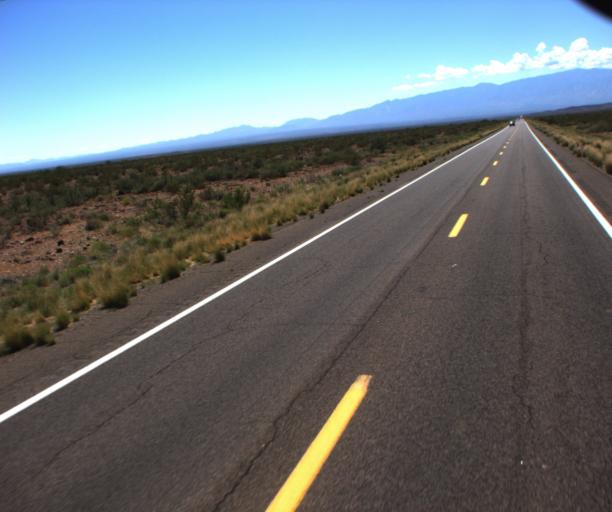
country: US
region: Arizona
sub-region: Greenlee County
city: Morenci
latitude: 32.8347
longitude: -109.4402
